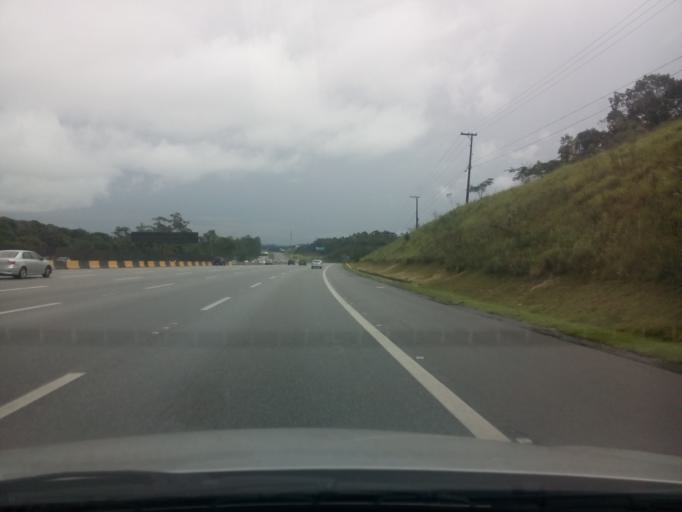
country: BR
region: Sao Paulo
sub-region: Sao Bernardo Do Campo
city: Sao Bernardo do Campo
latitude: -23.8187
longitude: -46.5826
